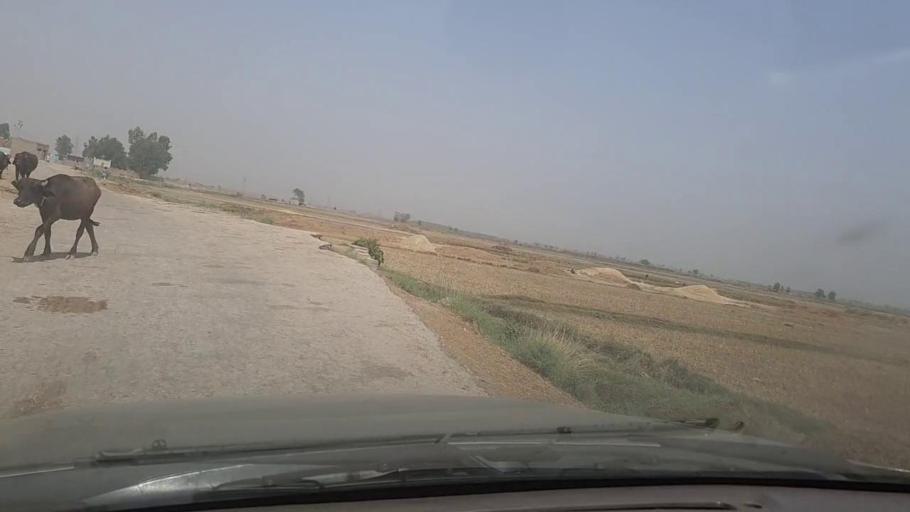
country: PK
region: Sindh
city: Madeji
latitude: 27.8035
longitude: 68.4025
